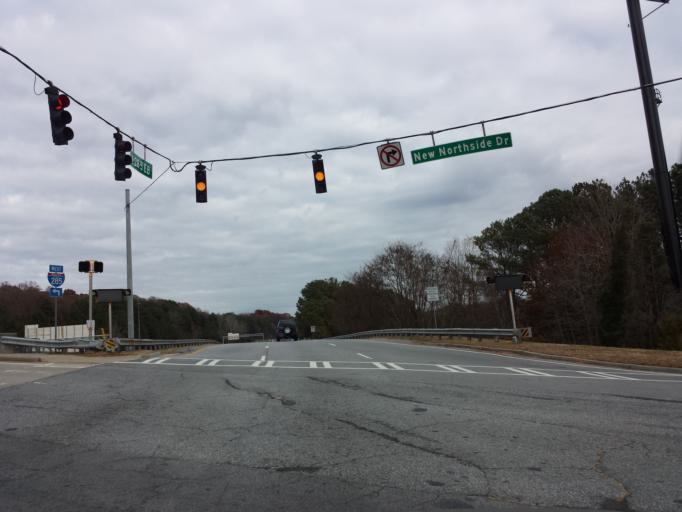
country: US
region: Georgia
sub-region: Fulton County
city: Sandy Springs
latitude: 33.9078
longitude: -84.4296
